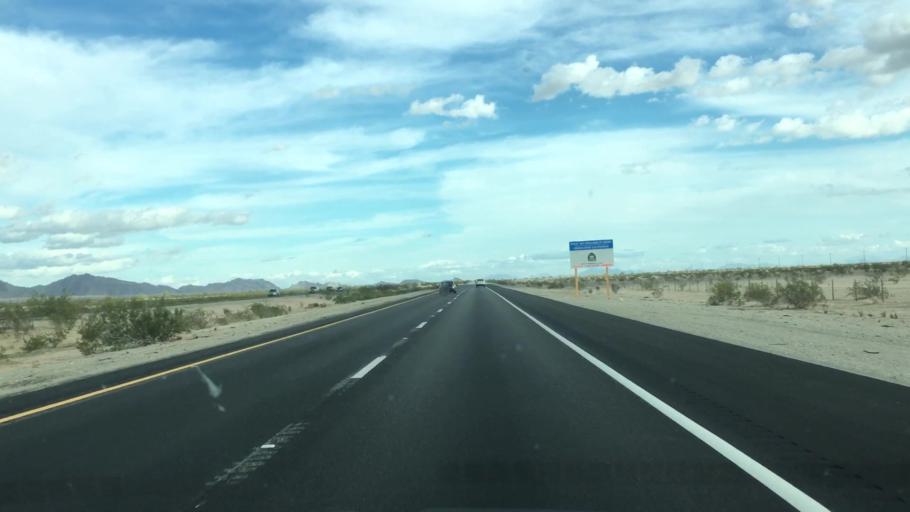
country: US
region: California
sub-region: Riverside County
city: Mesa Verde
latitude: 33.6087
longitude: -114.8783
